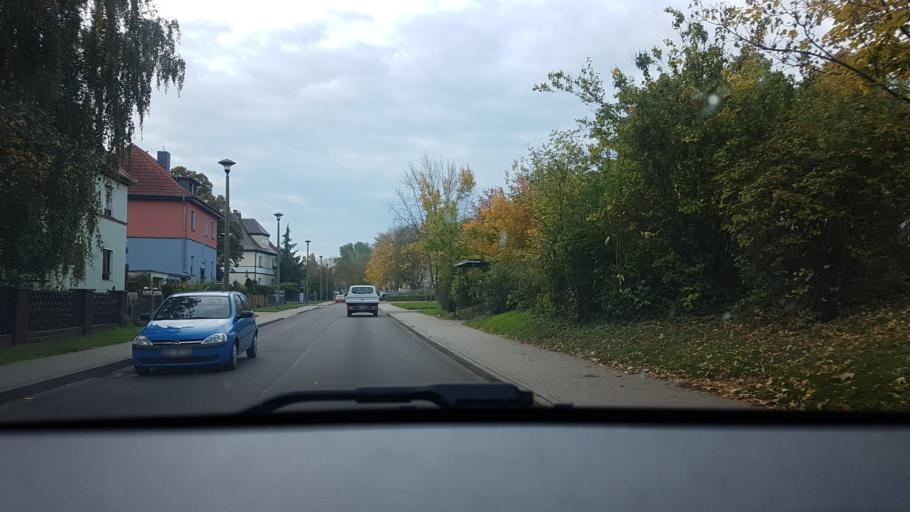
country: DE
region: Saxony-Anhalt
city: Bernburg
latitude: 51.7863
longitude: 11.7534
